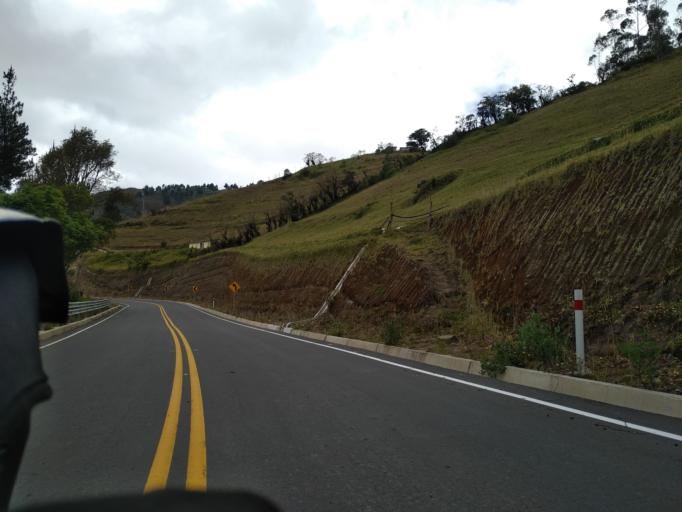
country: EC
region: Cotopaxi
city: Saquisili
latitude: -0.7526
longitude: -78.9077
